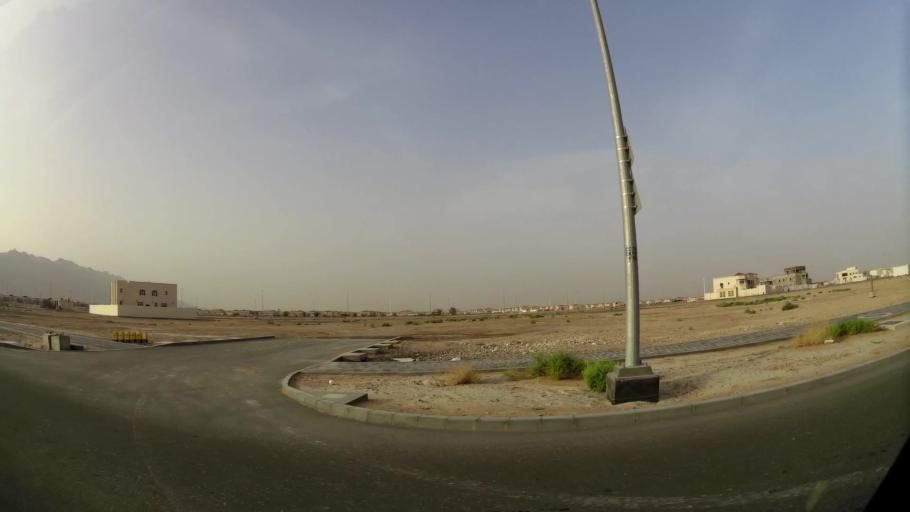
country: AE
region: Abu Dhabi
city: Al Ain
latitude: 24.1039
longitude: 55.7102
